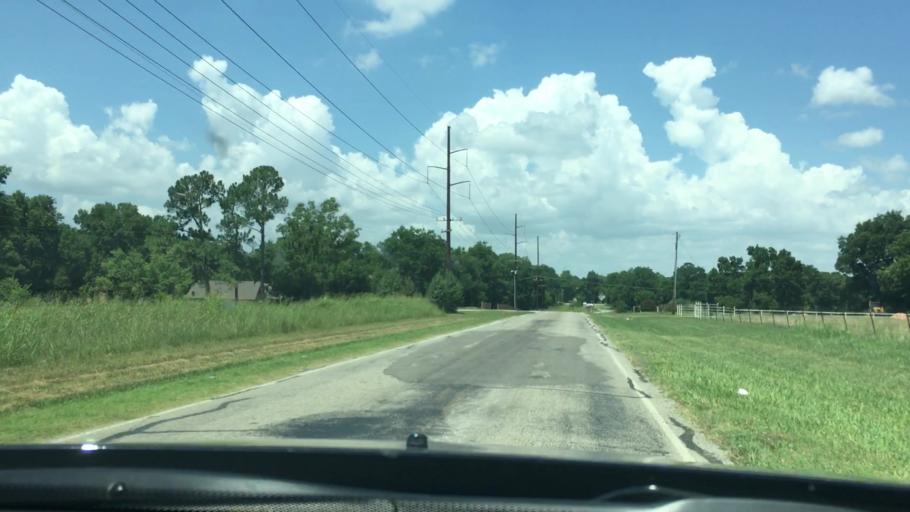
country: US
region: Oklahoma
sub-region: Pontotoc County
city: Ada
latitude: 34.6946
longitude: -96.5724
